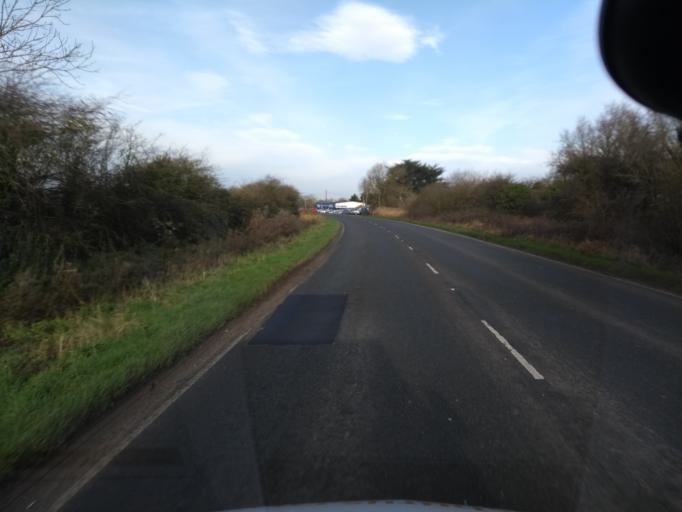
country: GB
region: England
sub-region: North Somerset
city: Bleadon
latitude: 51.2801
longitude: -2.9341
